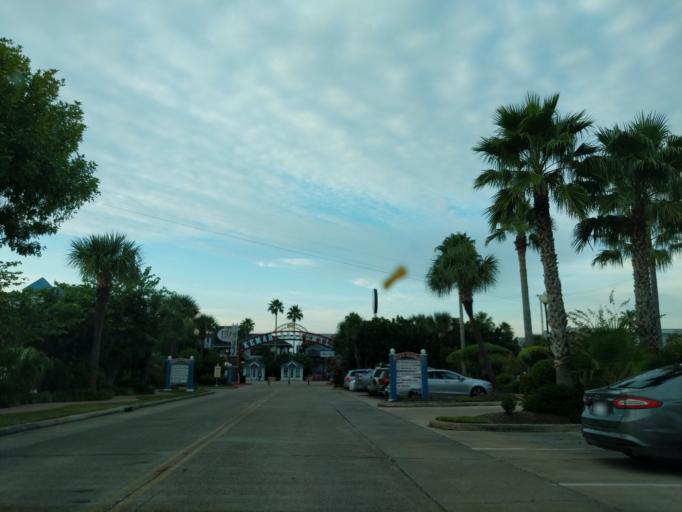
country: US
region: Texas
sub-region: Galveston County
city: Kemah
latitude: 29.5468
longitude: -95.0190
